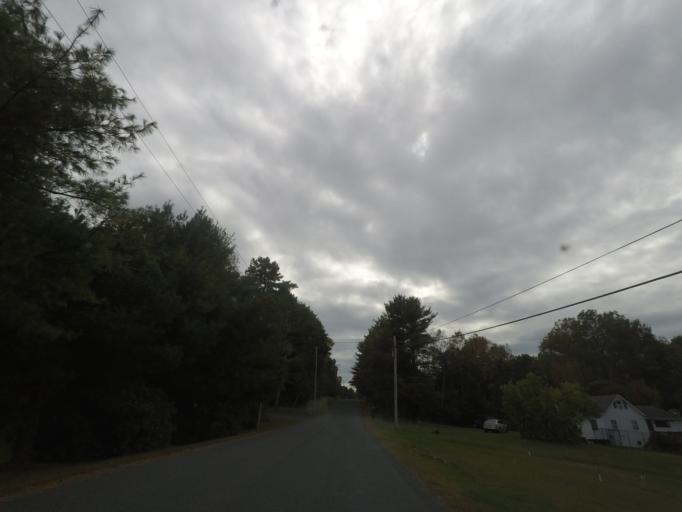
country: US
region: New York
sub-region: Rensselaer County
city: Nassau
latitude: 42.5513
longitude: -73.6426
